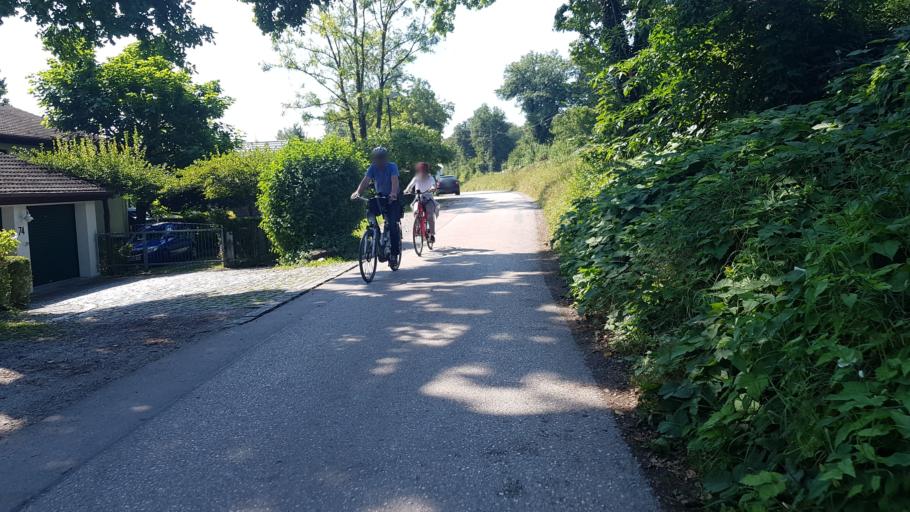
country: DE
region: Bavaria
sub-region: Upper Bavaria
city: Seefeld
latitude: 48.0309
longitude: 11.1871
